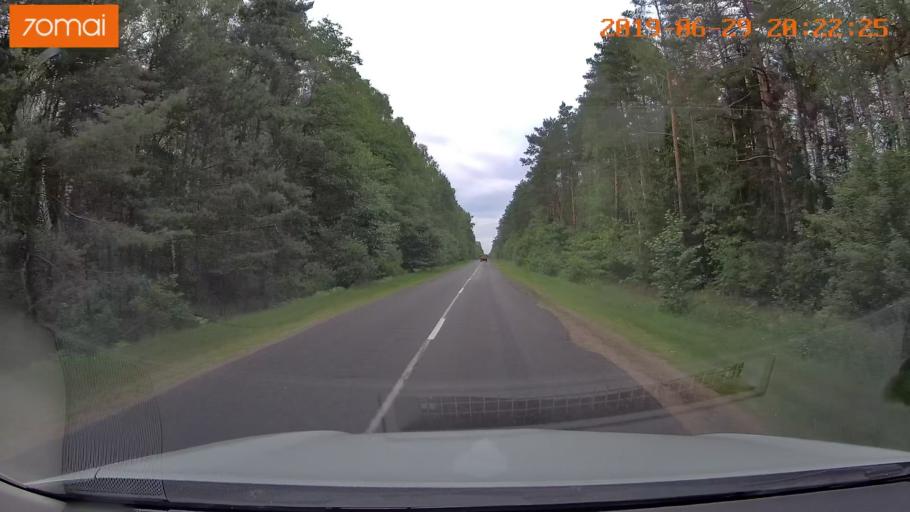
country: BY
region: Brest
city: Asnyezhytsy
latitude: 52.4317
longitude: 26.2545
